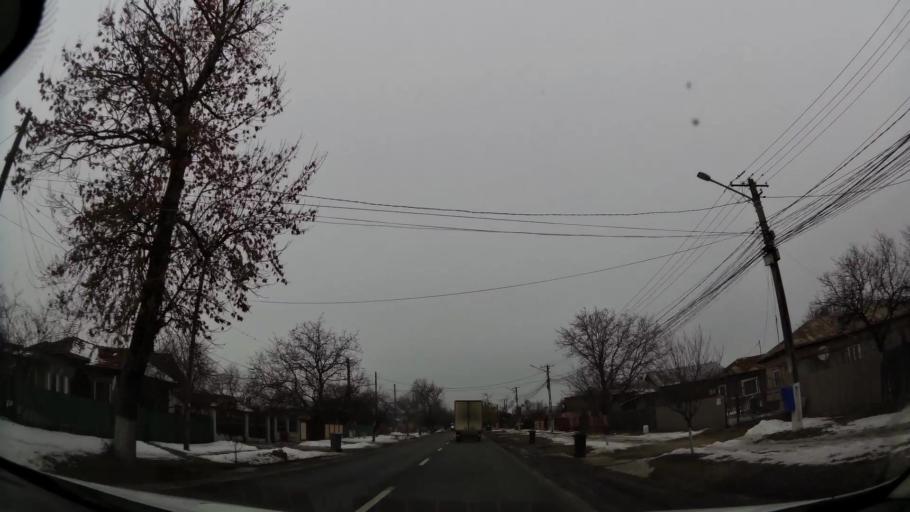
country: RO
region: Dambovita
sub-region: Comuna Tartasesti
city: Baldana
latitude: 44.6159
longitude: 25.7624
